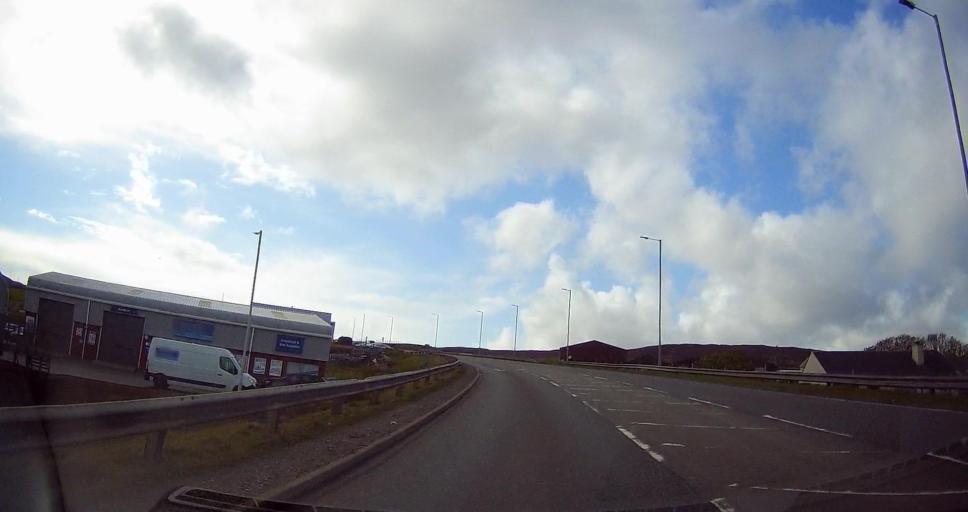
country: GB
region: Scotland
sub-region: Shetland Islands
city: Lerwick
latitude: 60.1698
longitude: -1.1683
